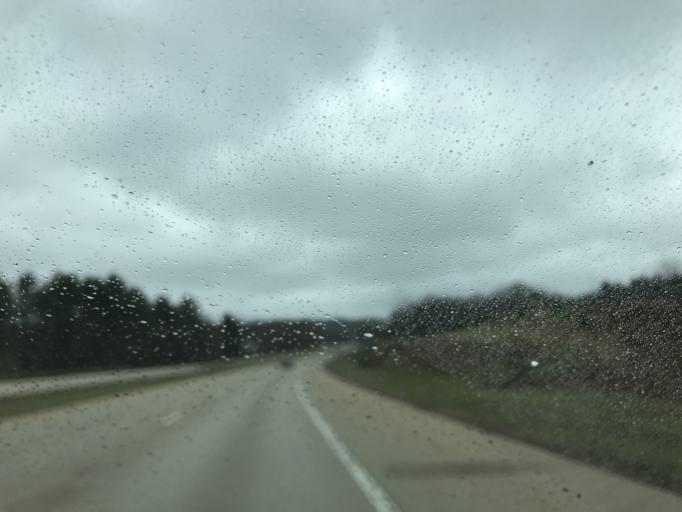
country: US
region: West Virginia
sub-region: Raleigh County
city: Daniels
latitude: 37.7730
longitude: -81.0543
